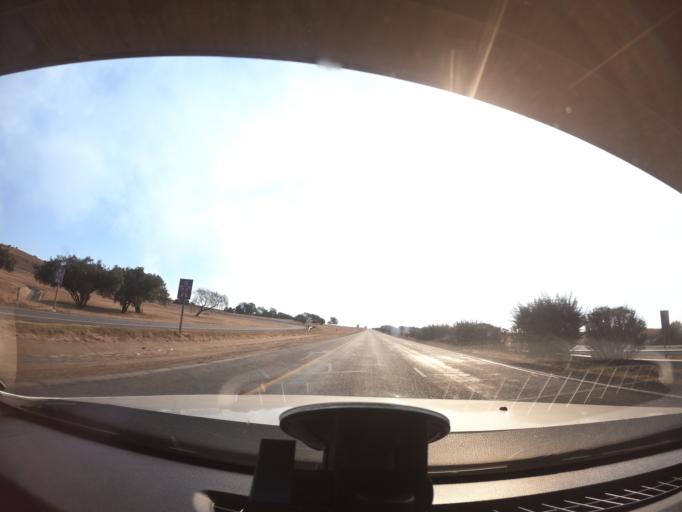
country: ZA
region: Gauteng
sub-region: Sedibeng District Municipality
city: Heidelberg
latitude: -26.4682
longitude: 28.3414
